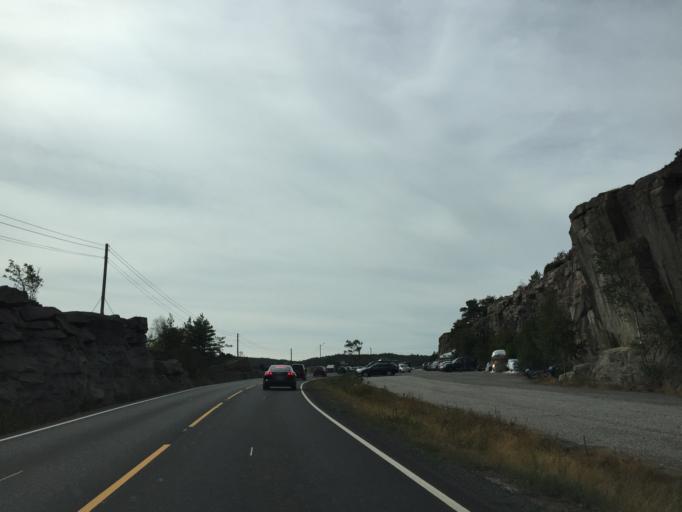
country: NO
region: Ostfold
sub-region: Fredrikstad
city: Fredrikstad
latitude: 59.1268
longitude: 10.9231
